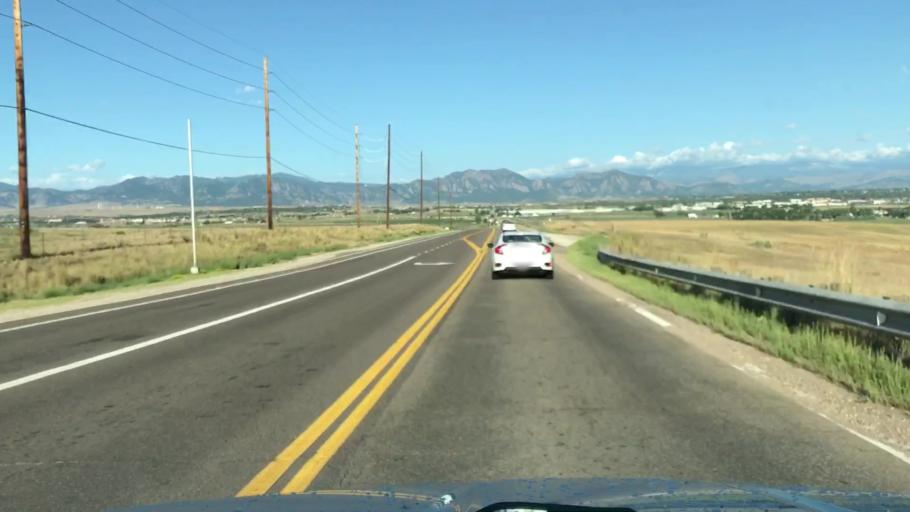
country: US
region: Colorado
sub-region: Broomfield County
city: Broomfield
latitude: 39.9568
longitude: -105.0720
